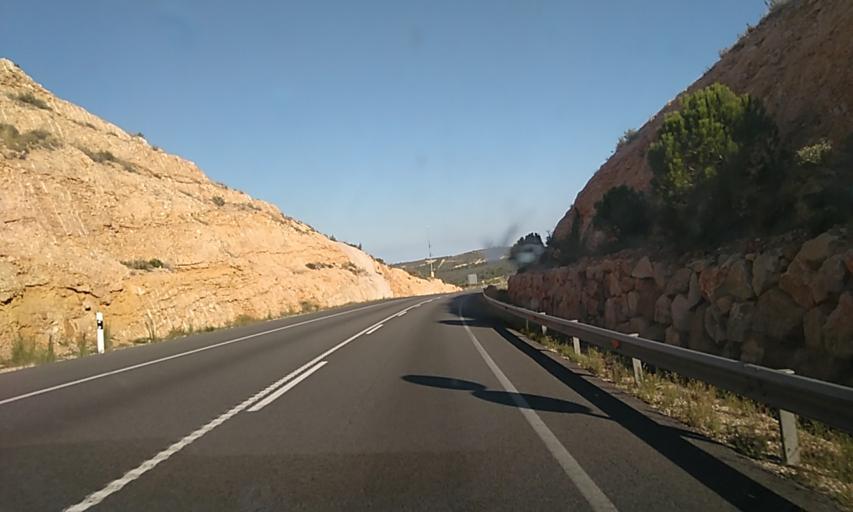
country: ES
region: Valencia
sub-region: Provincia de Castello
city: Torreblanca
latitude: 40.2115
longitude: 0.1244
